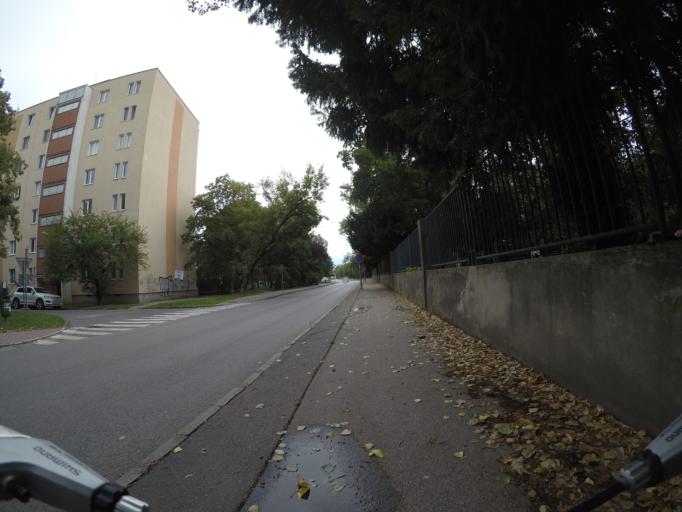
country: SK
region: Bratislavsky
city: Bratislava
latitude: 48.1622
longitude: 17.1622
